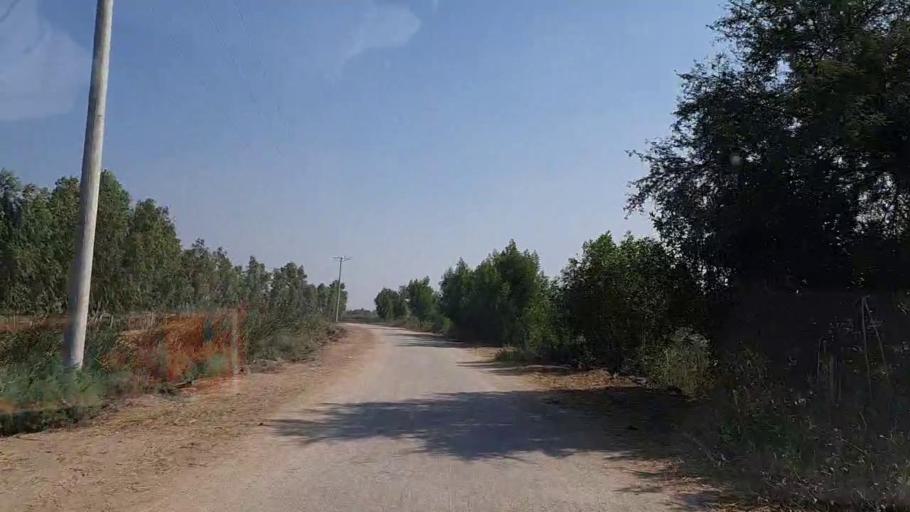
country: PK
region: Sindh
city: Thatta
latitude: 24.7994
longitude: 67.9668
